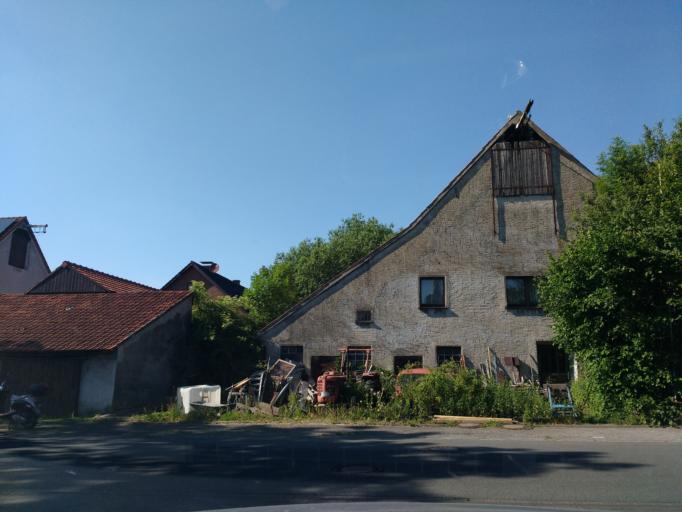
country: DE
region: North Rhine-Westphalia
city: Bad Lippspringe
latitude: 51.7642
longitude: 8.7783
